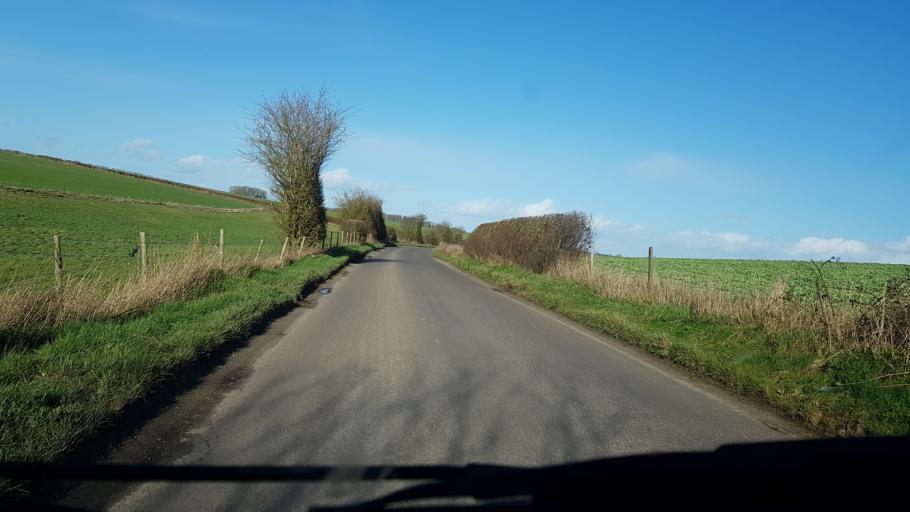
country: GB
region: England
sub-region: Wiltshire
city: Huish
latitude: 51.3942
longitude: -1.8148
